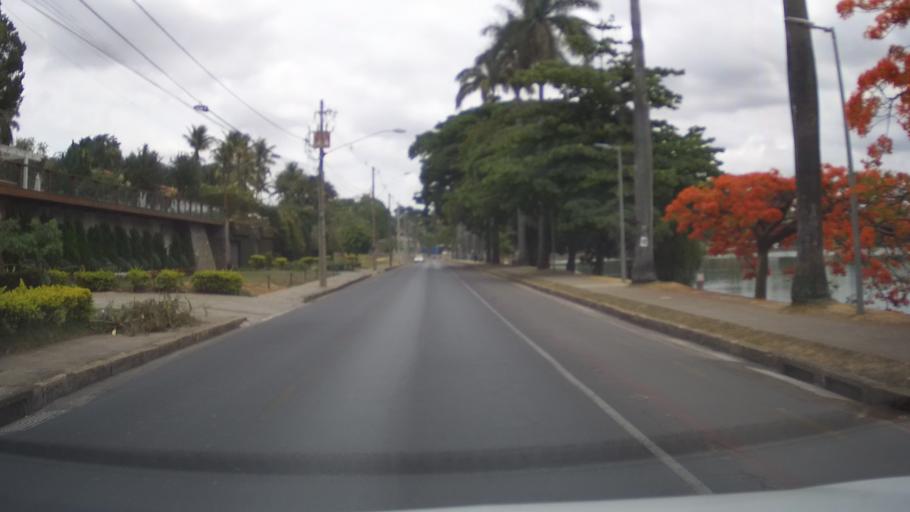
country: BR
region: Minas Gerais
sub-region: Belo Horizonte
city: Belo Horizonte
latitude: -19.8516
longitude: -43.9678
